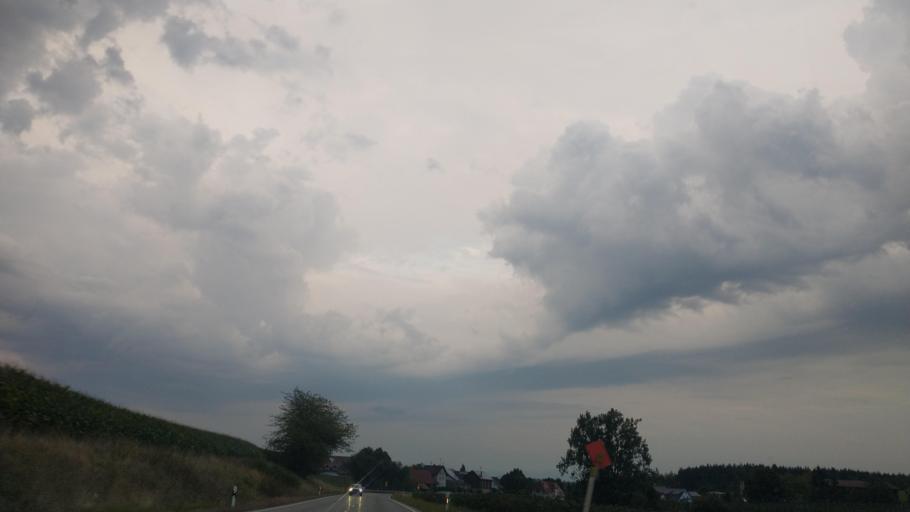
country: DE
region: Baden-Wuerttemberg
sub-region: Tuebingen Region
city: Tettnang
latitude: 47.6642
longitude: 9.6243
